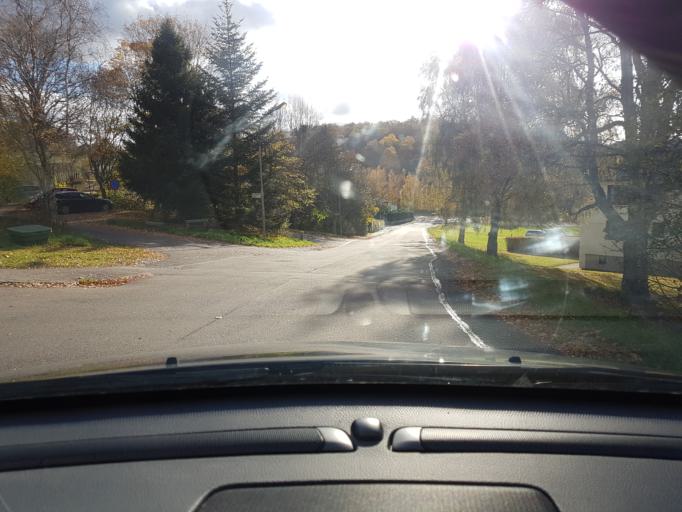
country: SE
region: Vaestra Goetaland
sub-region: Ale Kommun
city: Surte
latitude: 57.8307
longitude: 12.0216
